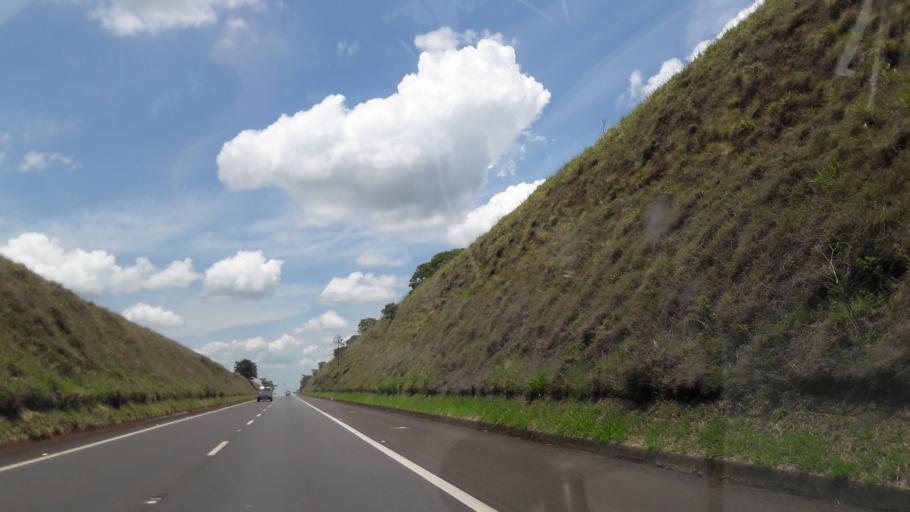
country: BR
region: Sao Paulo
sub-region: Avare
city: Avare
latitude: -22.9551
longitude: -48.8343
